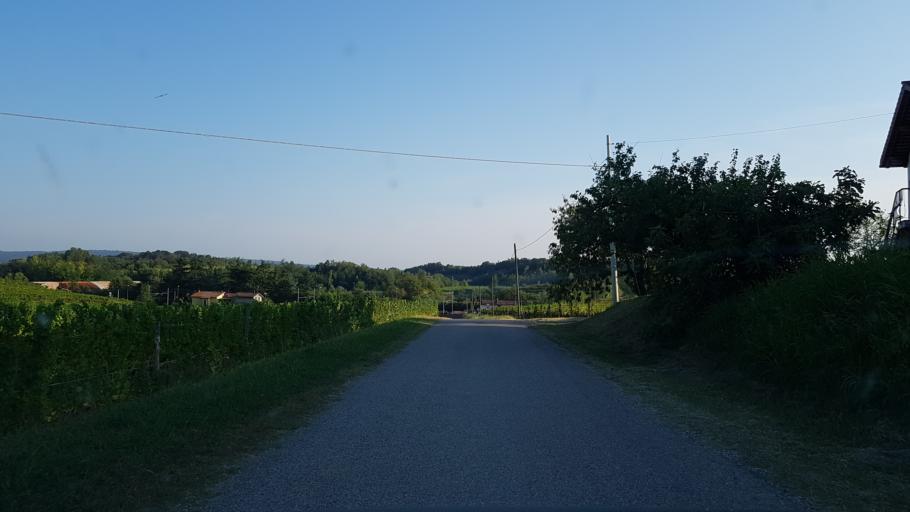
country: IT
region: Friuli Venezia Giulia
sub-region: Provincia di Gorizia
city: Cormons
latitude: 45.9490
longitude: 13.4844
